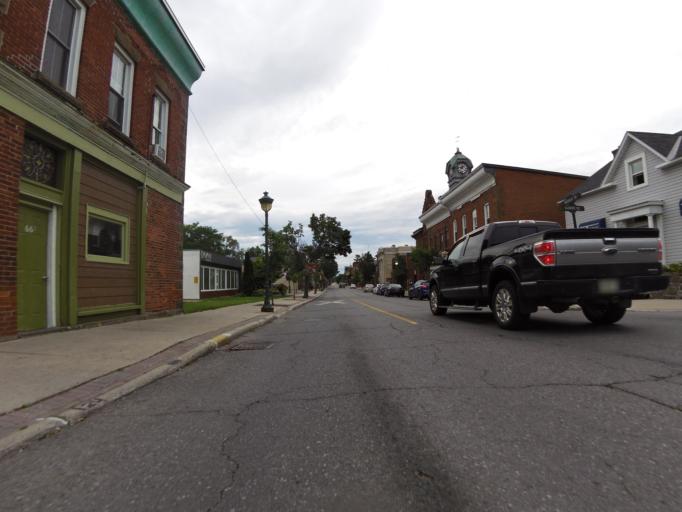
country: CA
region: Ontario
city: Carleton Place
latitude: 45.1382
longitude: -76.1440
